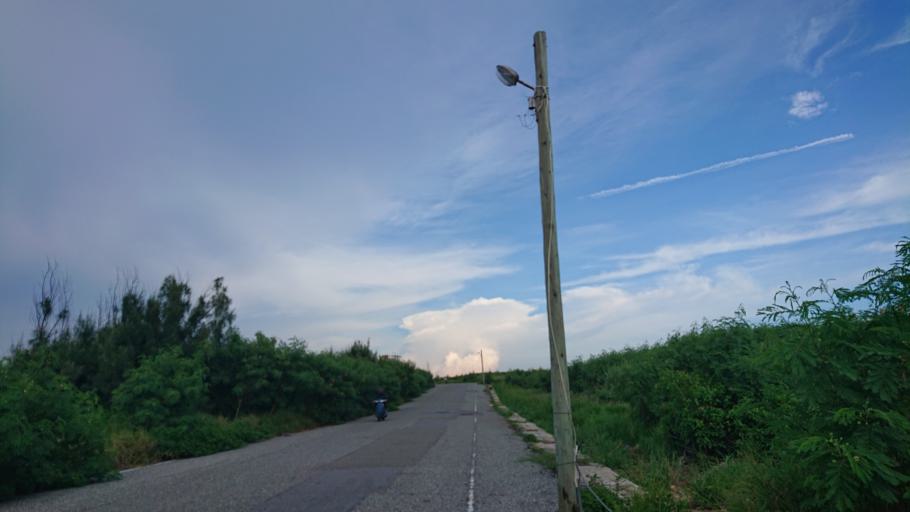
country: TW
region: Taiwan
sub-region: Penghu
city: Ma-kung
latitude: 23.5222
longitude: 119.6049
